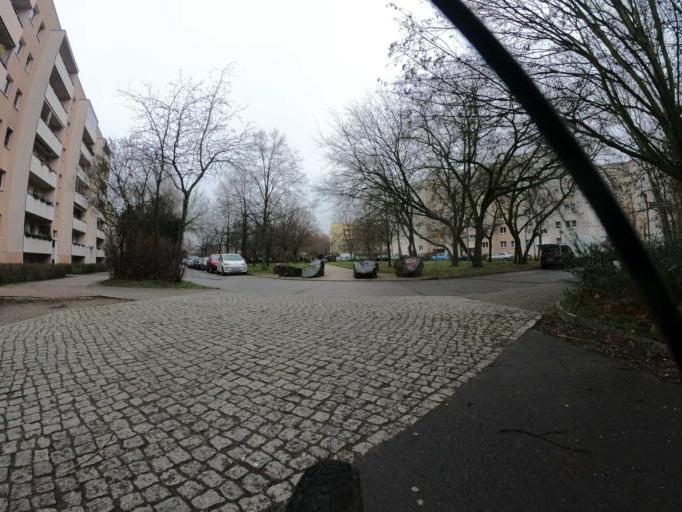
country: DE
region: Berlin
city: Marzahn
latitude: 52.5581
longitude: 13.5665
